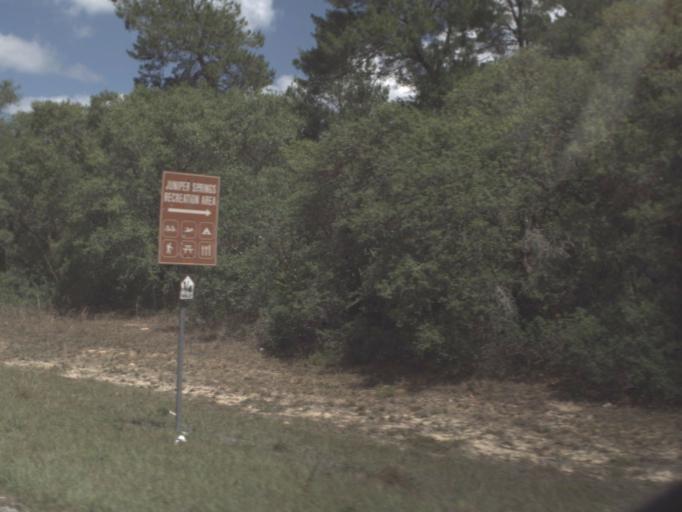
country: US
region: Florida
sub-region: Lake County
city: Astor
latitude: 29.1781
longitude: -81.7069
